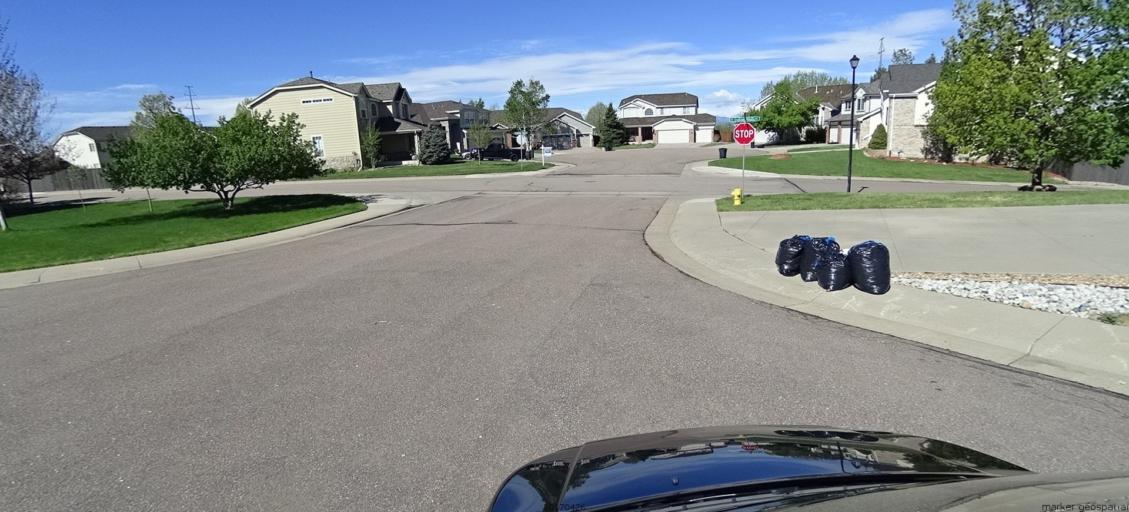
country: US
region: Colorado
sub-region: Douglas County
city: Carriage Club
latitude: 39.5384
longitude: -104.9027
